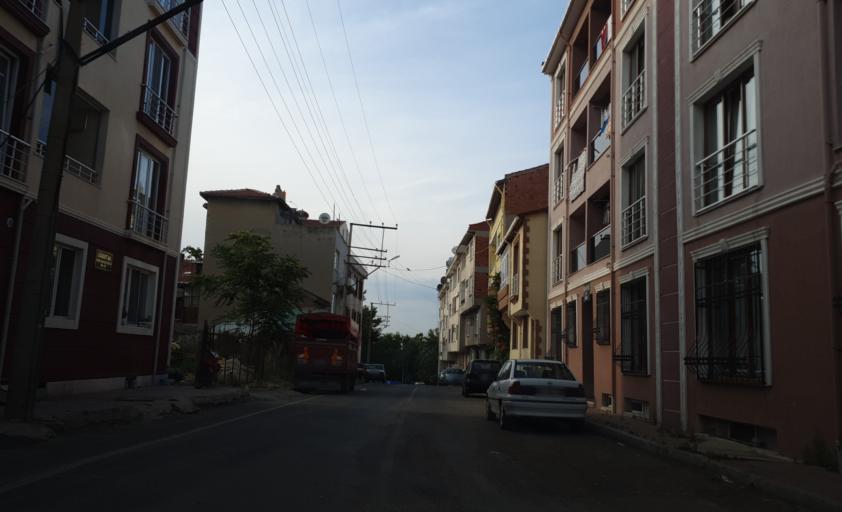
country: TR
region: Tekirdag
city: Hayrabolu
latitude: 41.2163
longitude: 27.1092
